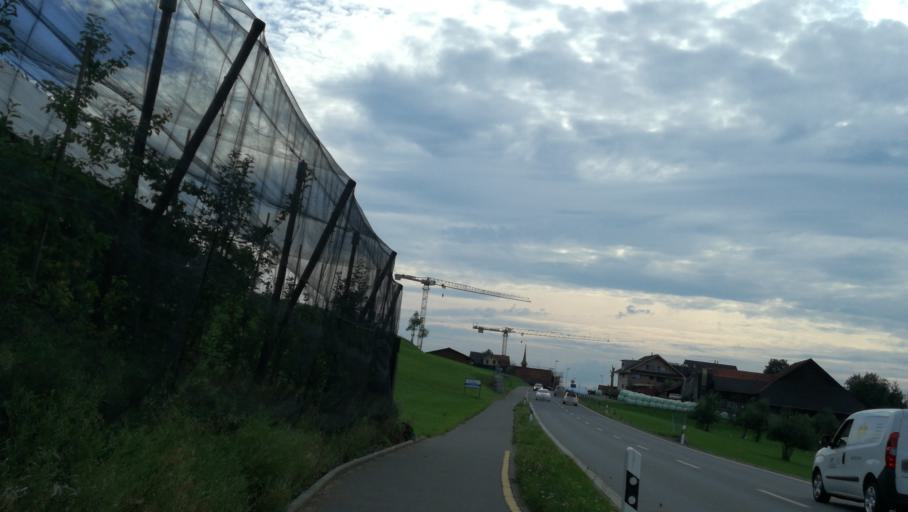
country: CH
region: Lucerne
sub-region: Lucerne-Land District
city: Root
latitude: 47.1342
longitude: 8.4103
